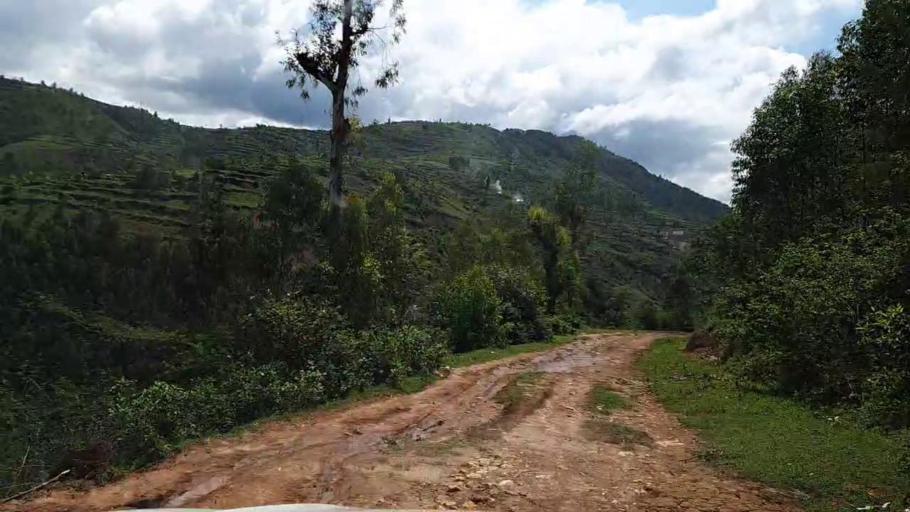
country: RW
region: Southern Province
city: Gikongoro
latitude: -2.3615
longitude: 29.5425
